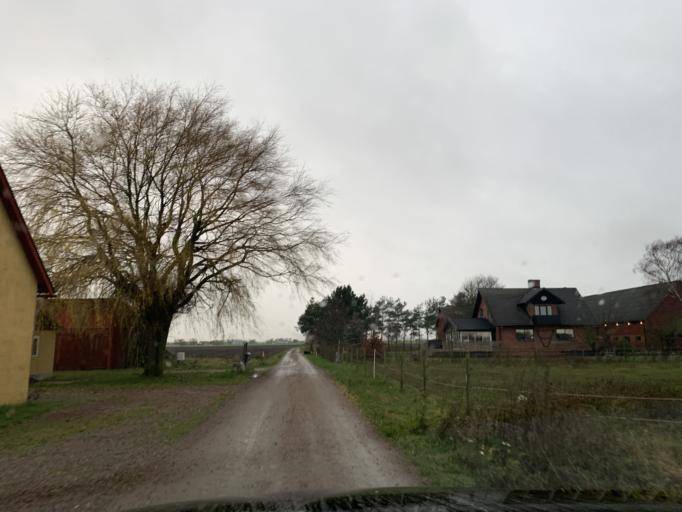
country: SE
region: Skane
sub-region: Kavlinge Kommun
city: Hofterup
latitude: 55.8469
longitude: 12.9918
